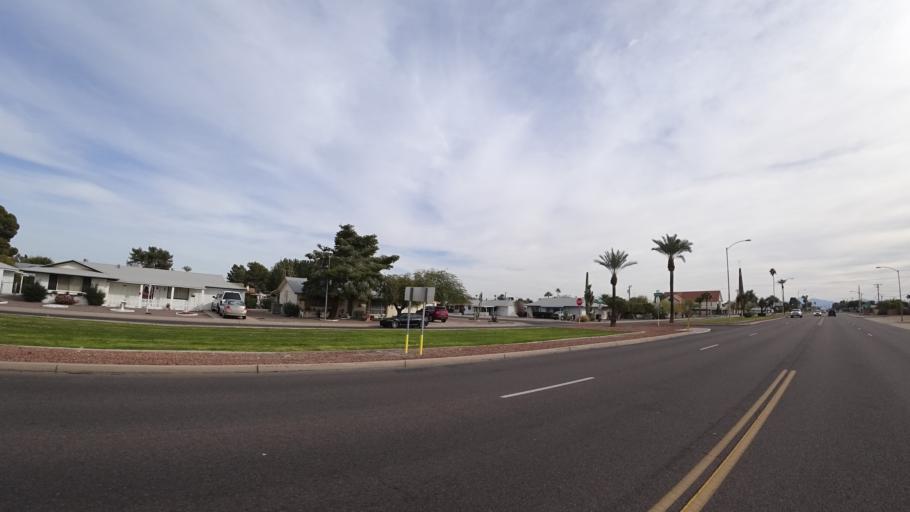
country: US
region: Arizona
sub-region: Maricopa County
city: Youngtown
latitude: 33.5864
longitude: -112.2988
